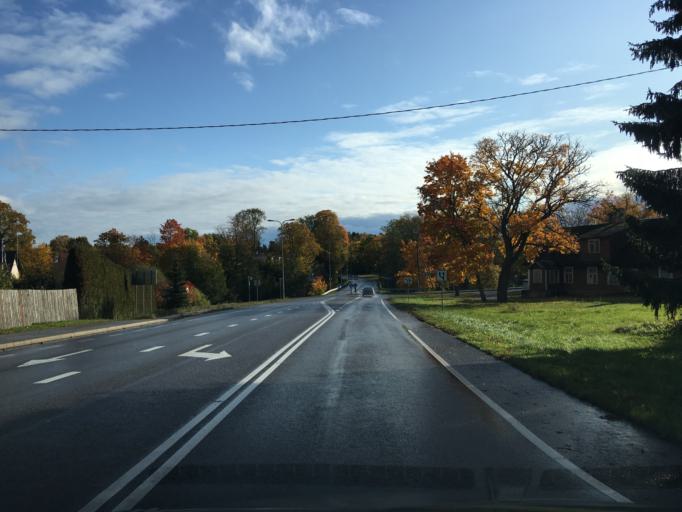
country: EE
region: Harju
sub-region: Raasiku vald
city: Raasiku
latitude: 59.1866
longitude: 25.1647
